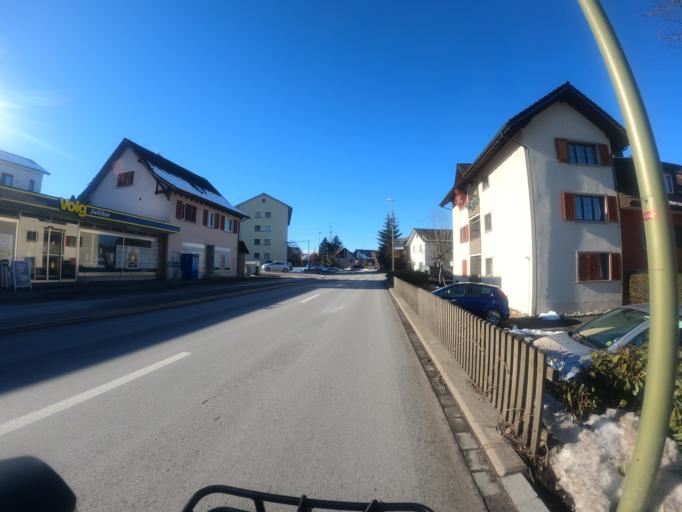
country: CH
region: Zurich
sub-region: Bezirk Affoltern
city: Hedingen
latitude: 47.2875
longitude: 8.4319
